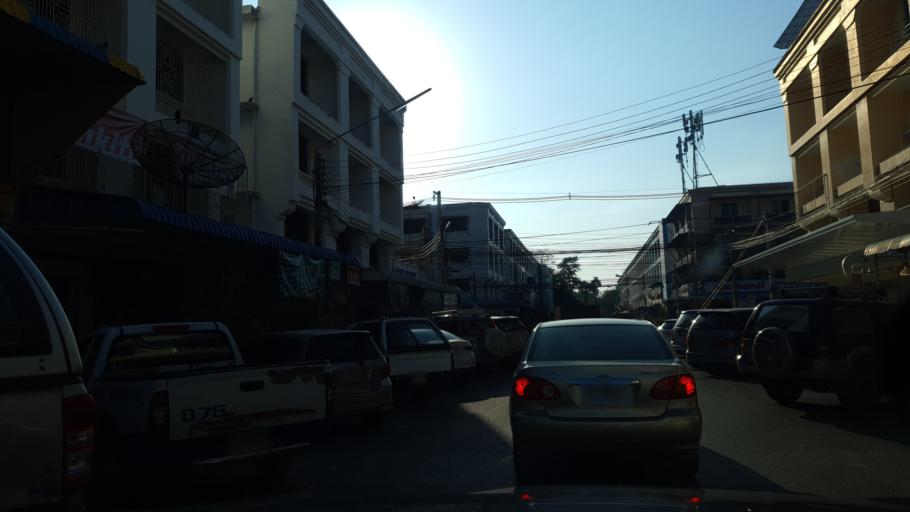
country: TH
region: Krabi
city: Krabi
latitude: 8.0661
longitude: 98.9155
